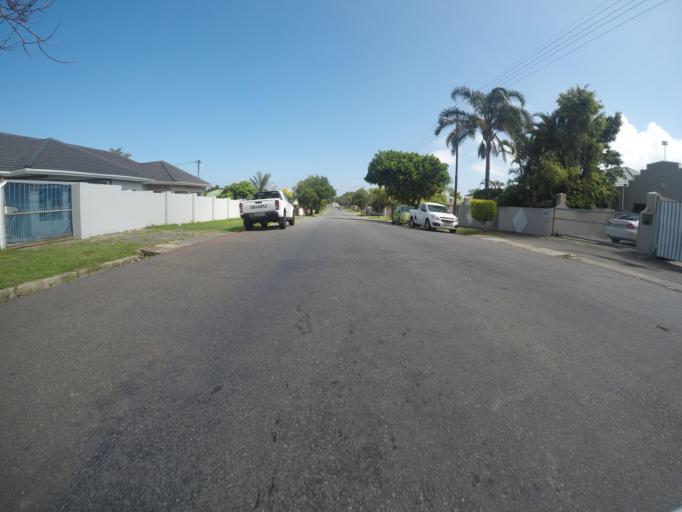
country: ZA
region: Eastern Cape
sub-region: Buffalo City Metropolitan Municipality
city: East London
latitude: -32.9795
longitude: 27.9112
